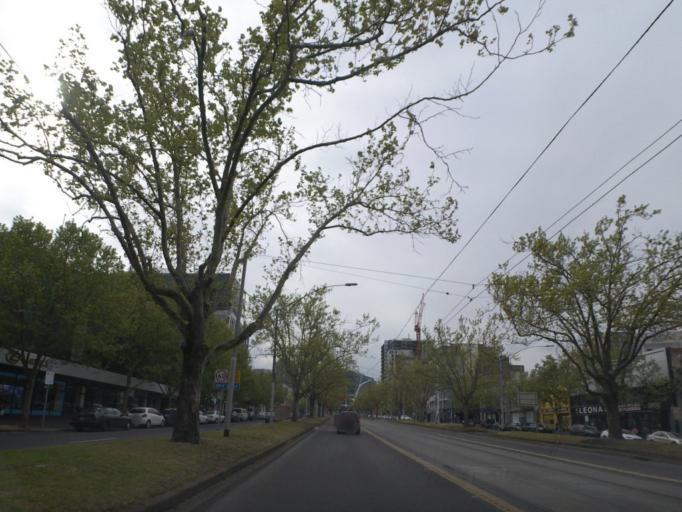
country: AU
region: Victoria
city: Carlton
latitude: -37.8054
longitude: 144.9590
